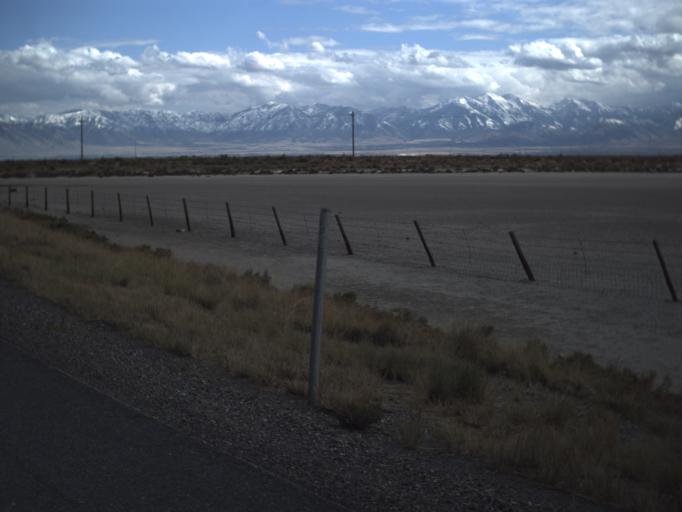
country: US
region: Utah
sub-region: Tooele County
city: Grantsville
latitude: 40.7061
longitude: -112.5209
